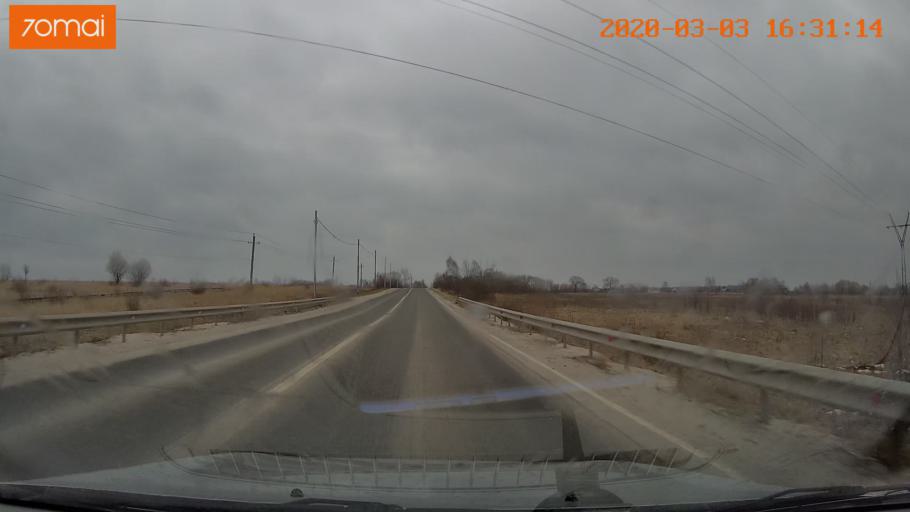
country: RU
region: Moskovskaya
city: Konobeyevo
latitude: 55.4269
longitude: 38.7220
